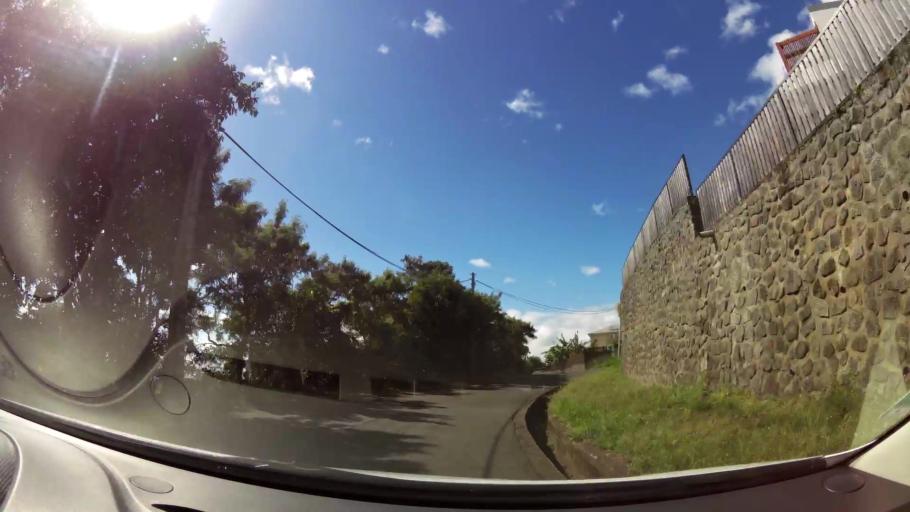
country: RE
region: Reunion
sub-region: Reunion
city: Sainte-Marie
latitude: -20.9186
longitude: 55.4977
